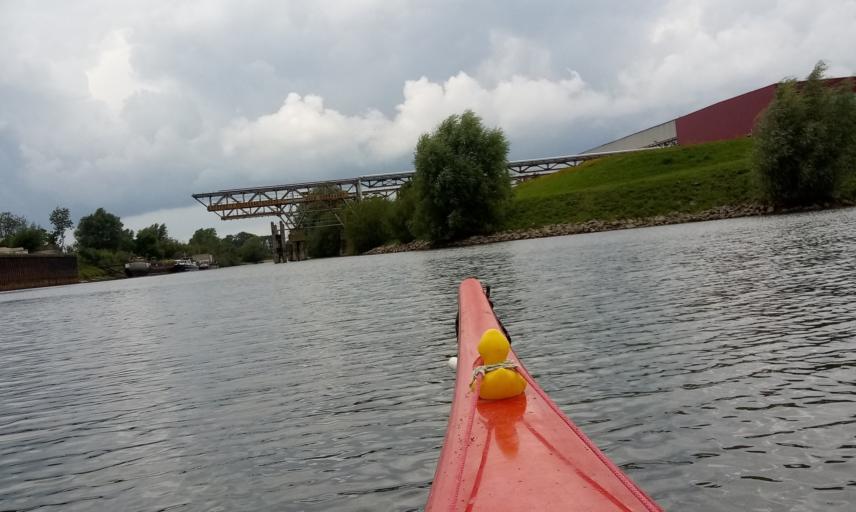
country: NL
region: Gelderland
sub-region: Gemeente Zutphen
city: Zutphen
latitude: 52.1559
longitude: 6.1939
